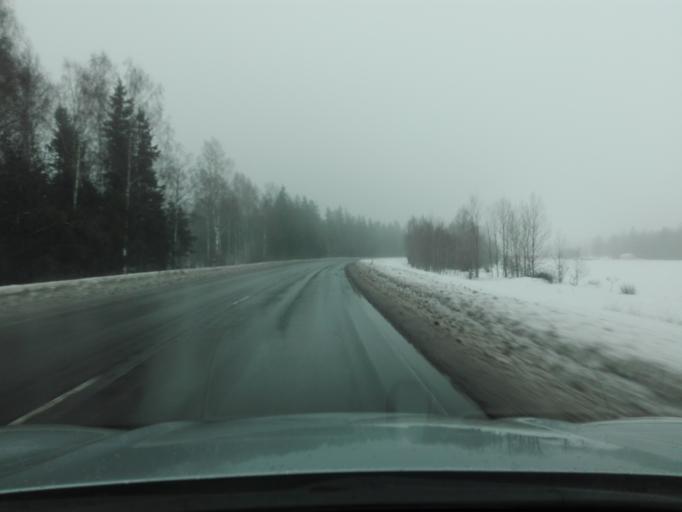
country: EE
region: Raplamaa
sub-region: Kohila vald
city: Kohila
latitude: 59.2284
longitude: 24.7765
